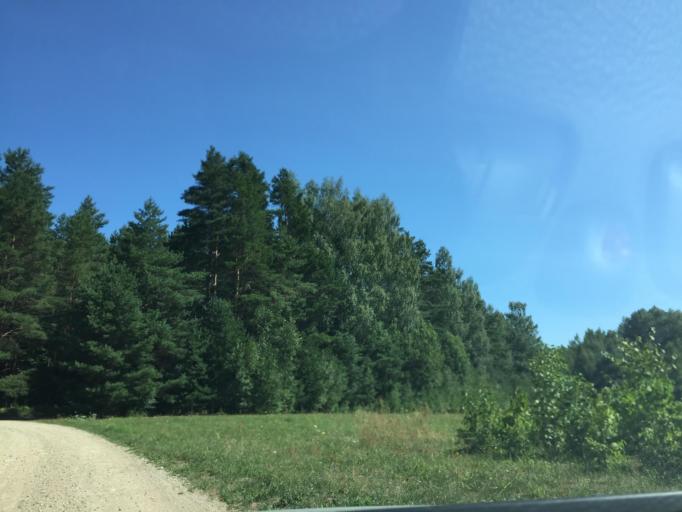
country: LV
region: Talsu Rajons
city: Stende
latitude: 57.1655
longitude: 22.2986
